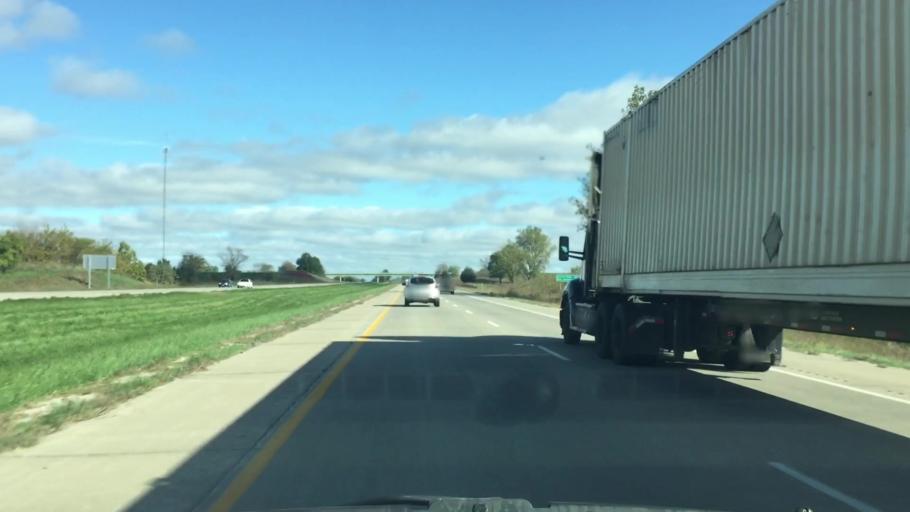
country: US
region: Iowa
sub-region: Decatur County
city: Leon
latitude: 40.7511
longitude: -93.8388
